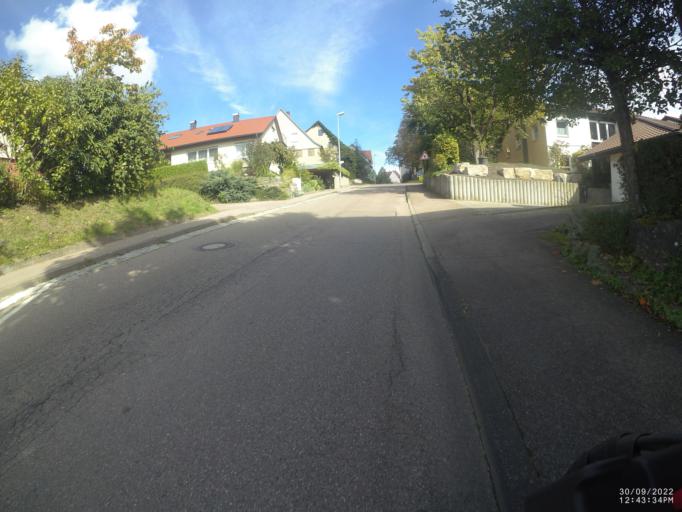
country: DE
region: Baden-Wuerttemberg
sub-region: Regierungsbezirk Stuttgart
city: Adelberg
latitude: 48.7609
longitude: 9.5990
